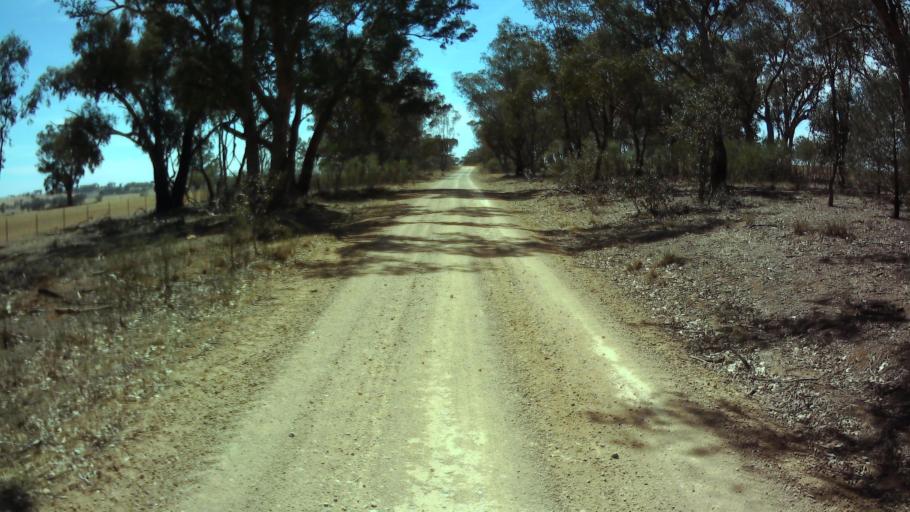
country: AU
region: New South Wales
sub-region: Weddin
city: Grenfell
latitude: -33.9422
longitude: 148.1396
